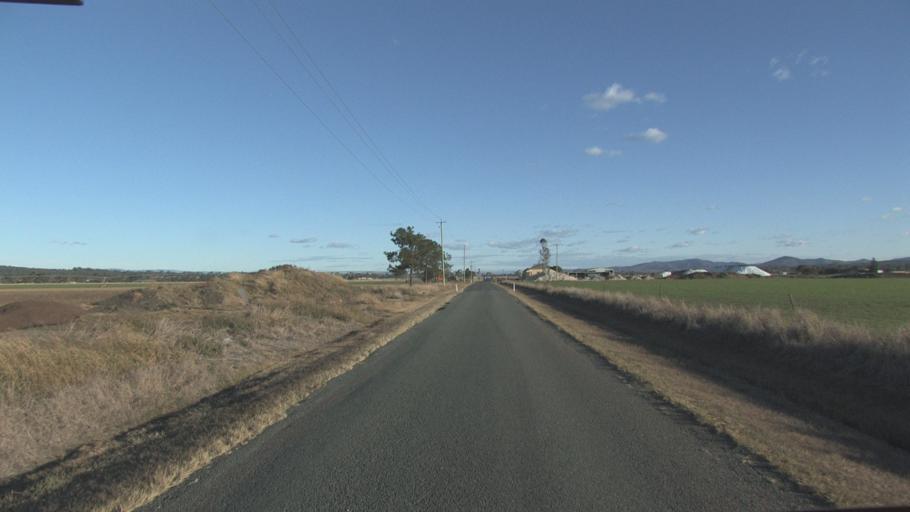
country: AU
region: Queensland
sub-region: Logan
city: Cedar Vale
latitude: -27.8551
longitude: 152.9601
